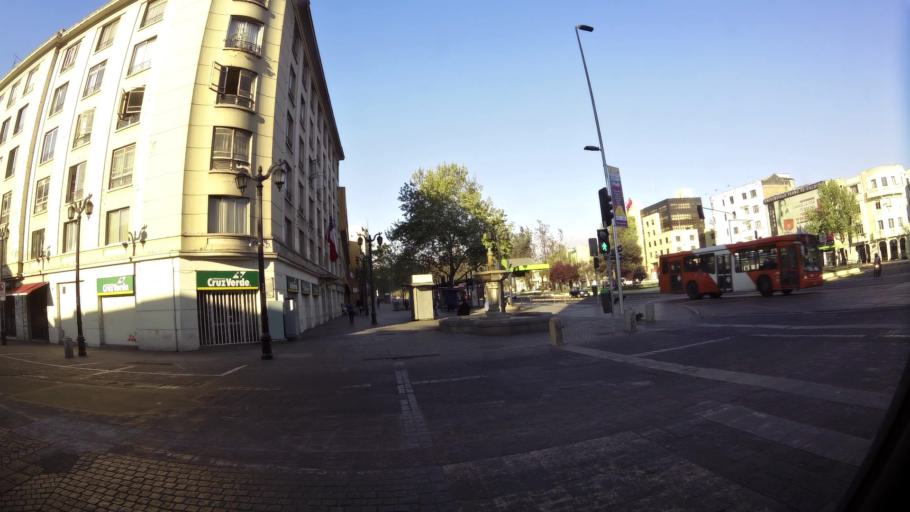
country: CL
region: Santiago Metropolitan
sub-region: Provincia de Santiago
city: Santiago
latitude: -33.4475
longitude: -70.6674
